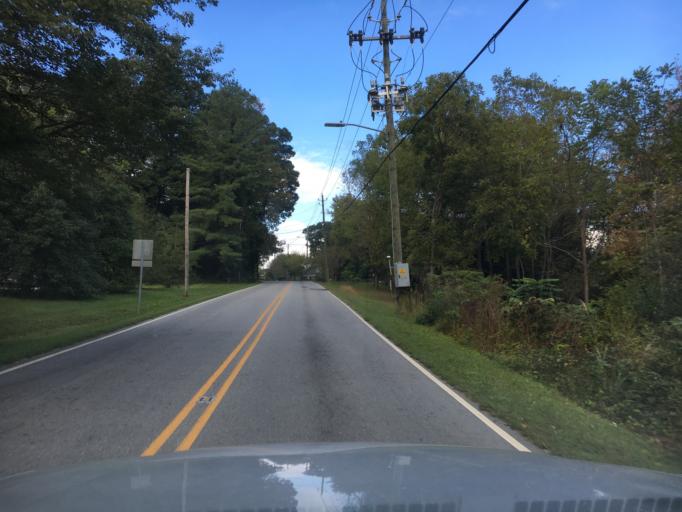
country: US
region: North Carolina
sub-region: Henderson County
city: Fletcher
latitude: 35.4310
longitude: -82.5031
